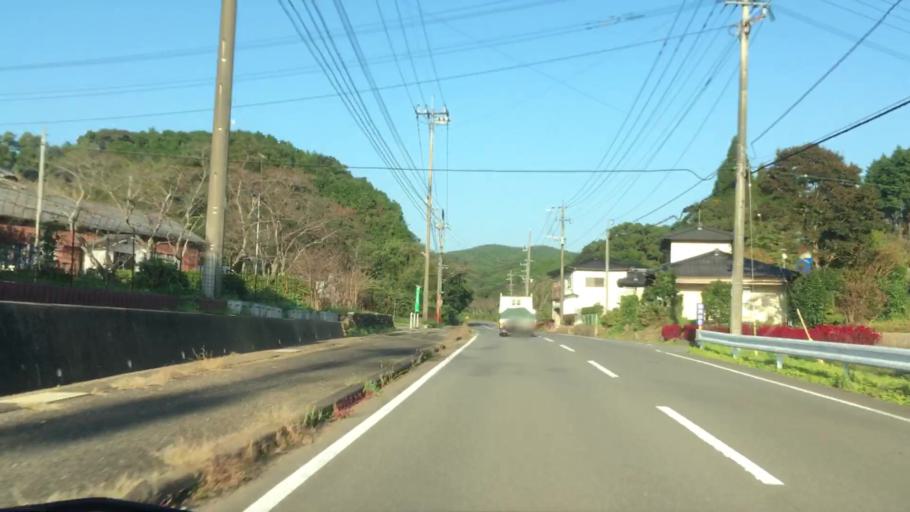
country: JP
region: Nagasaki
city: Togitsu
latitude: 32.9513
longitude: 129.6725
